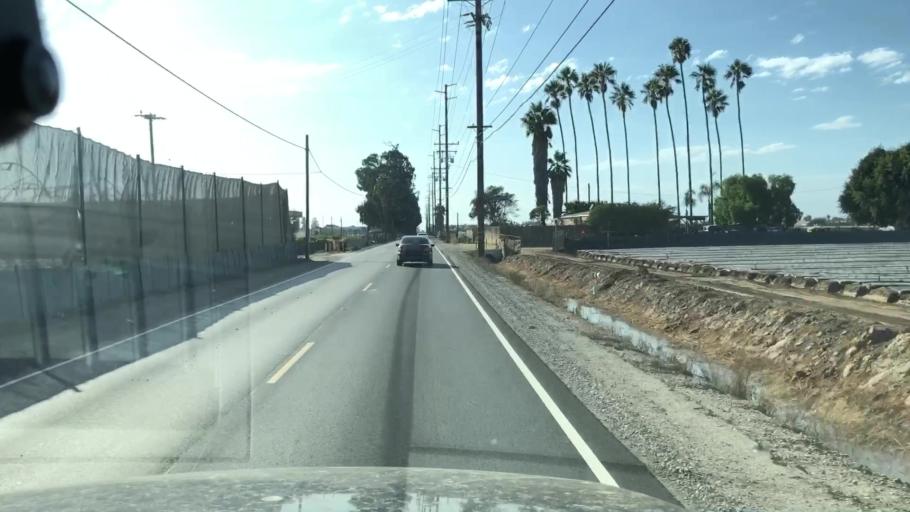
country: US
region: California
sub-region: Ventura County
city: Oxnard
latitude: 34.1898
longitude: -119.1490
